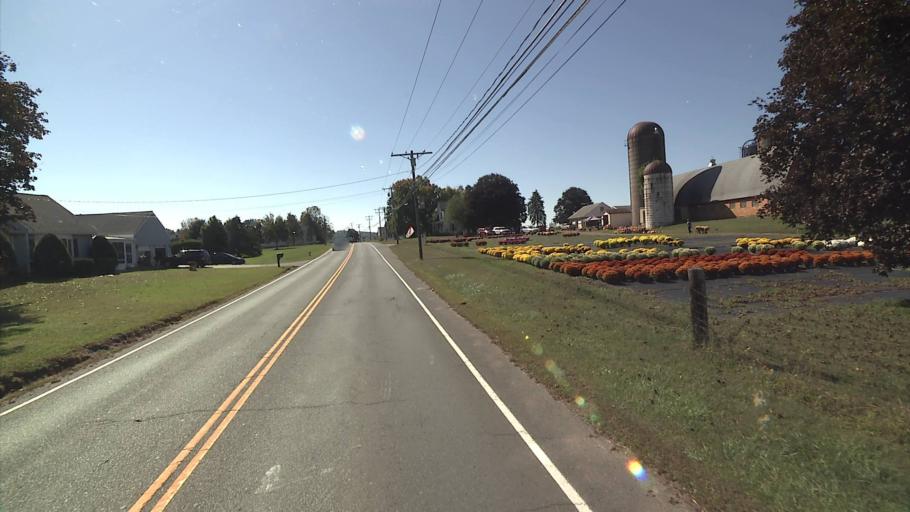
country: US
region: Connecticut
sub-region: Tolland County
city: Ellington
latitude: 41.8839
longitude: -72.4643
